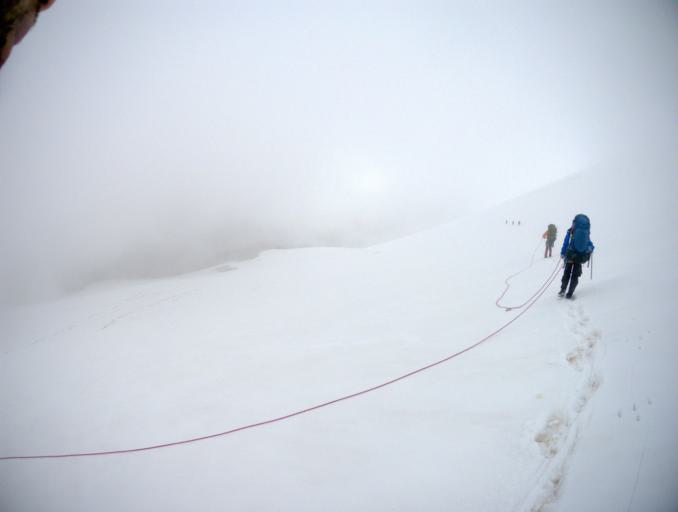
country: RU
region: Kabardino-Balkariya
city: Terskol
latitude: 43.3799
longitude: 42.4694
